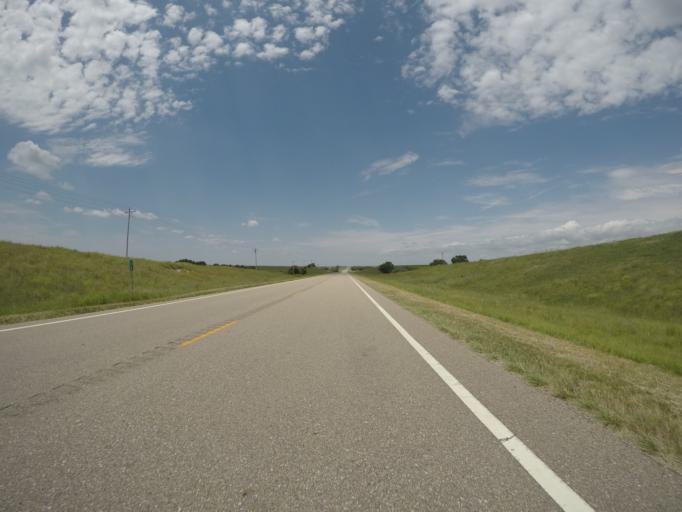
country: US
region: Kansas
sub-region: Graham County
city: Hill City
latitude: 39.3798
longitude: -99.6730
